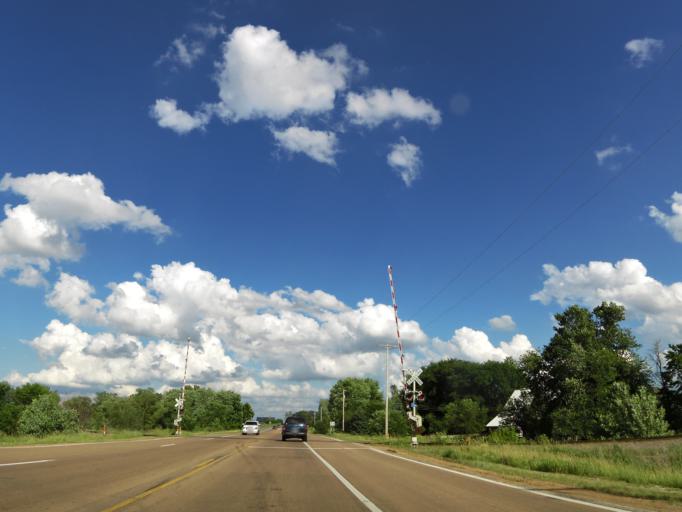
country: US
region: Minnesota
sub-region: Carver County
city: Victoria
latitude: 44.8109
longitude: -93.6662
